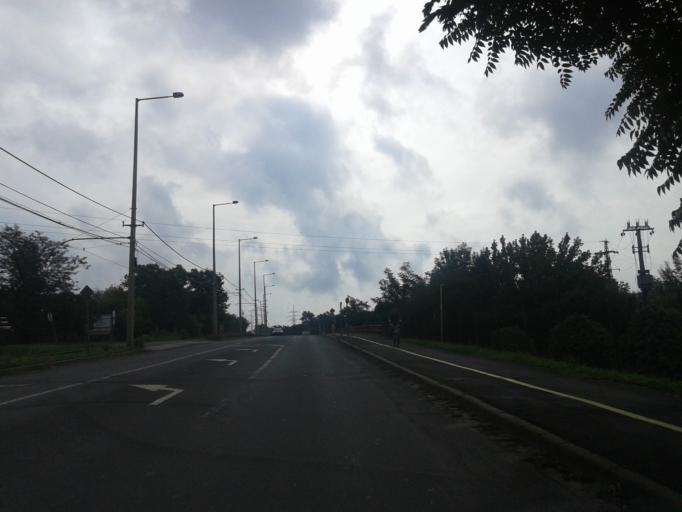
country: HU
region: Csongrad
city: Szeged
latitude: 46.2546
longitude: 20.1108
